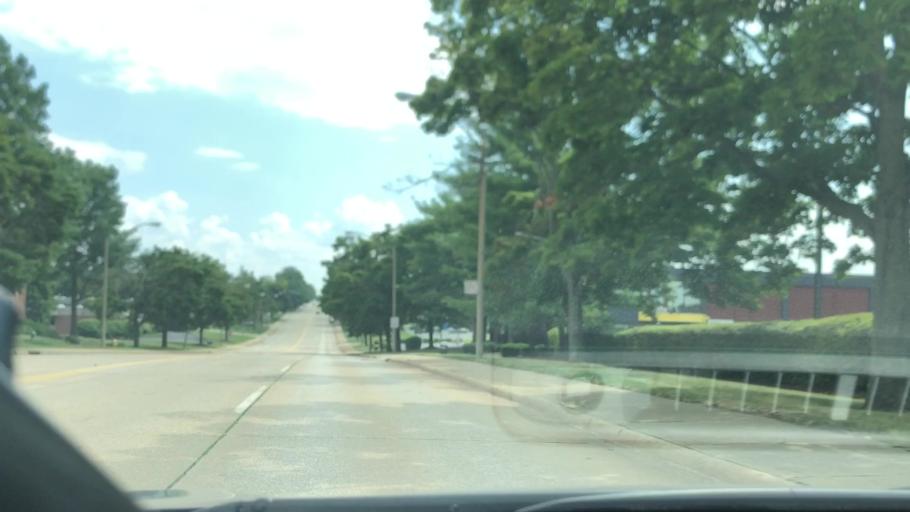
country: US
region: Ohio
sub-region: Summit County
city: Akron
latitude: 41.0709
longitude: -81.5205
